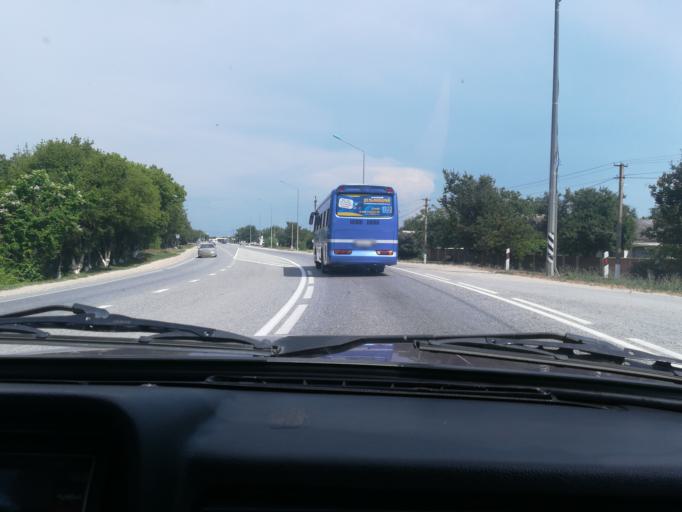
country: RU
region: Krasnodarskiy
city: Vinogradnyy
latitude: 45.0567
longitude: 37.3188
